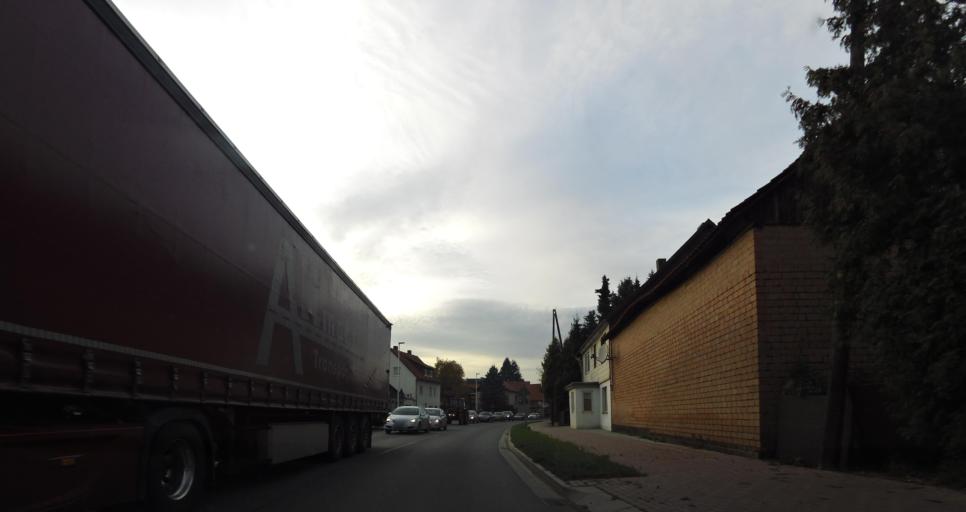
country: DE
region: Lower Saxony
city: Eimen
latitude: 51.8697
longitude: 9.8106
